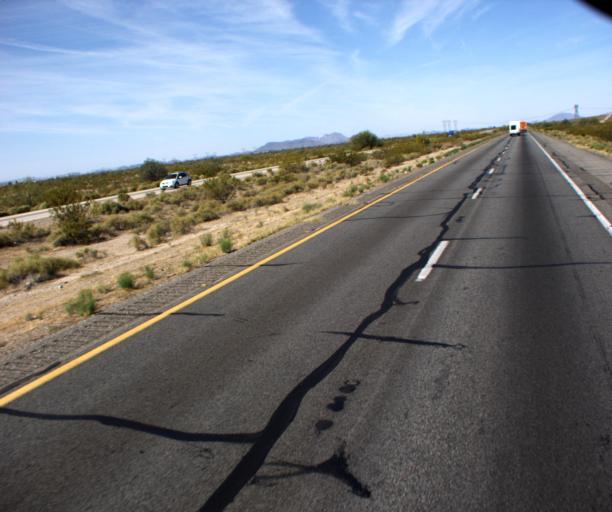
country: US
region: Arizona
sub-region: Maricopa County
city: Buckeye
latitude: 33.4485
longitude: -112.7176
